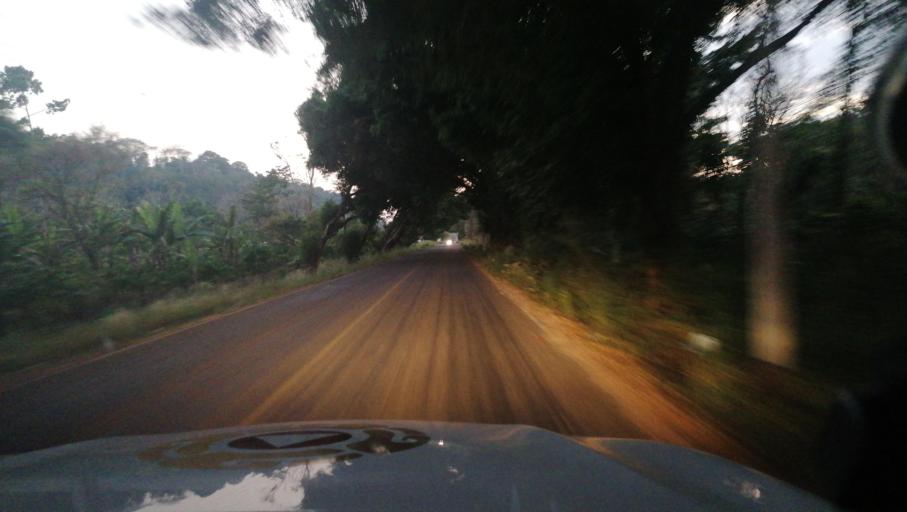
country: MX
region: Chiapas
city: Veinte de Noviembre
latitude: 14.9827
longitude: -92.2431
